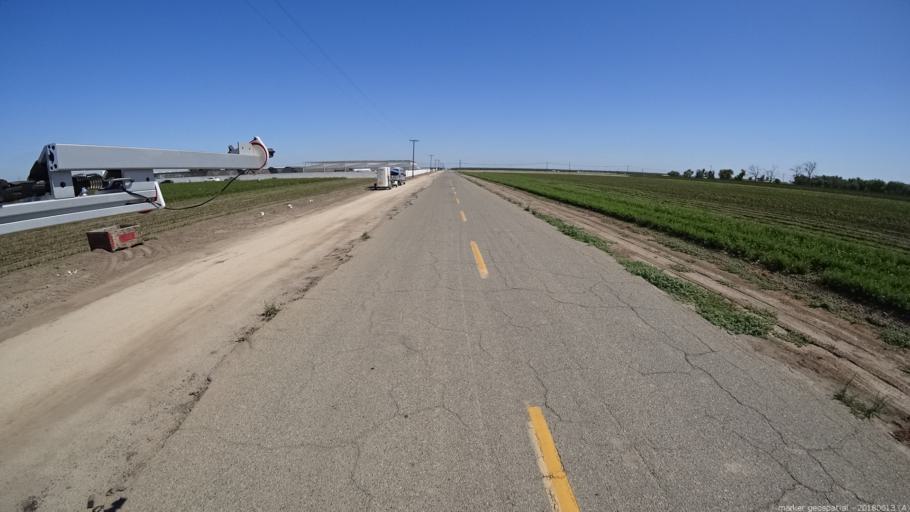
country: US
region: California
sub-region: Madera County
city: Chowchilla
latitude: 37.0664
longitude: -120.4011
